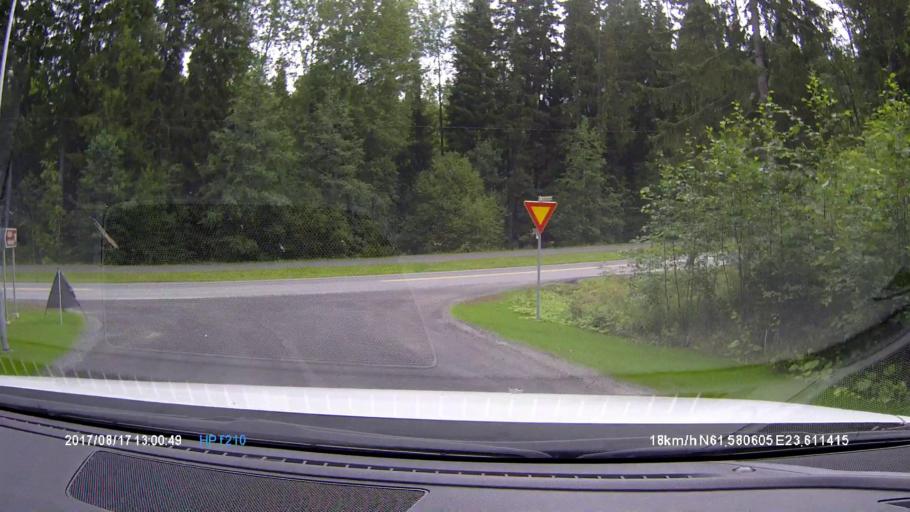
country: FI
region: Pirkanmaa
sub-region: Tampere
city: Yloejaervi
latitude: 61.5805
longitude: 23.6116
